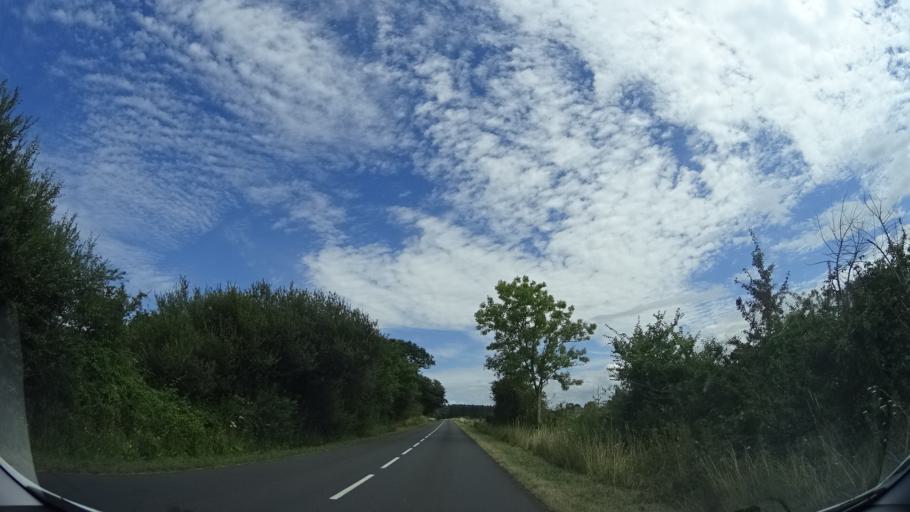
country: FR
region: Lower Normandy
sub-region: Departement de la Manche
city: Marcey-les-Greves
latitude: 48.6802
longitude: -1.4058
